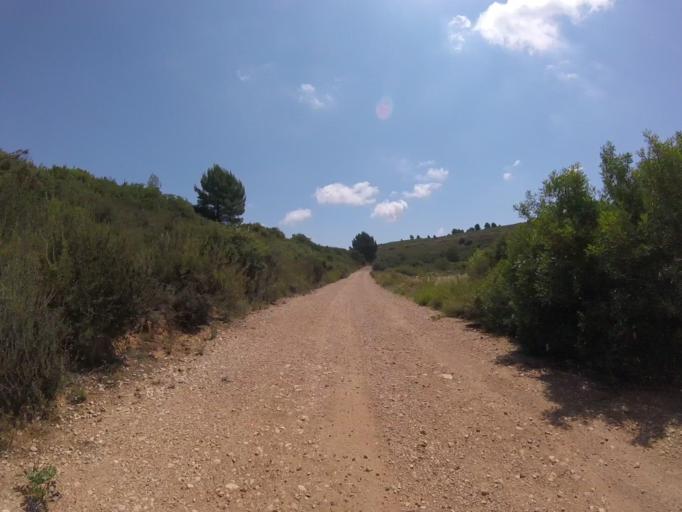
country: ES
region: Valencia
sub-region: Provincia de Castello
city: Torreblanca
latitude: 40.2134
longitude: 0.1443
